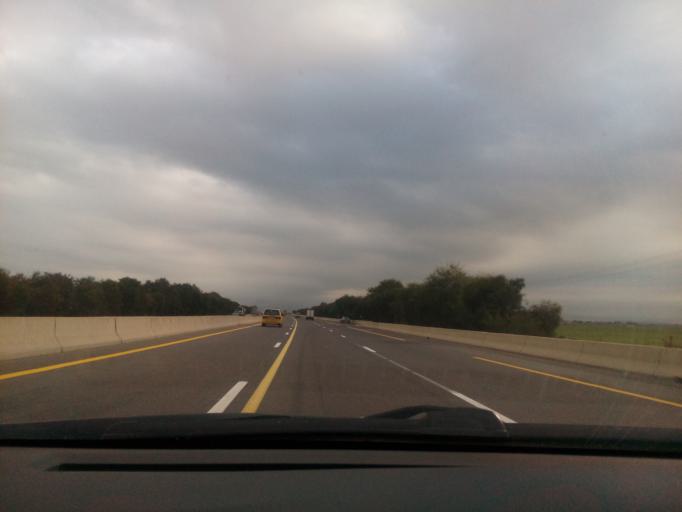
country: DZ
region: Relizane
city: Relizane
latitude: 35.7908
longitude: 0.4611
